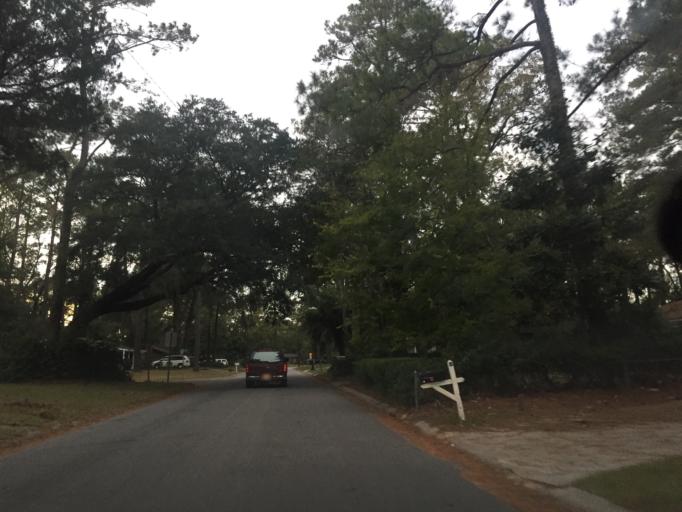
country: US
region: Georgia
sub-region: Chatham County
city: Montgomery
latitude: 31.9877
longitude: -81.1212
